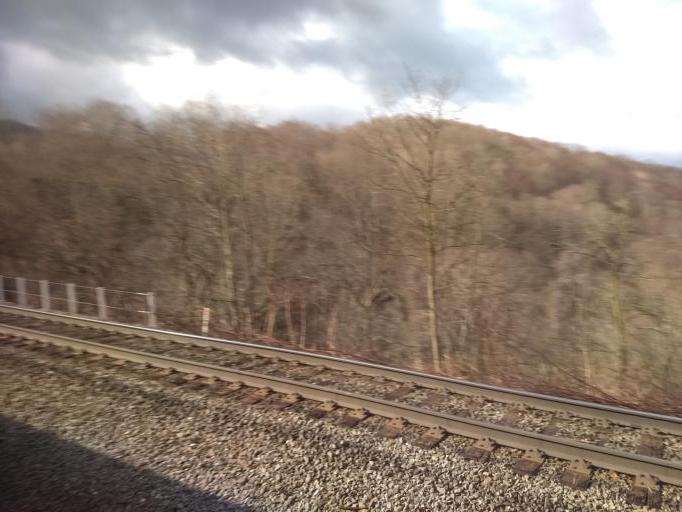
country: US
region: Pennsylvania
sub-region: Cambria County
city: Vinco
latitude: 40.3688
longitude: -78.8198
